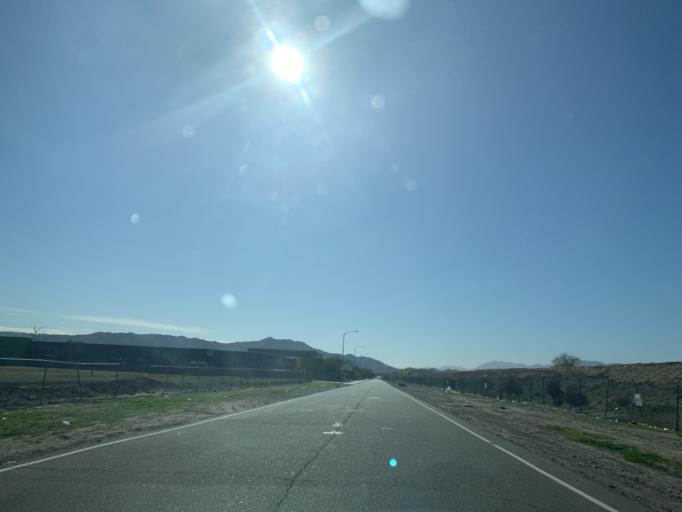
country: US
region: Arizona
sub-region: Maricopa County
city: Laveen
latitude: 33.4021
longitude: -112.1423
